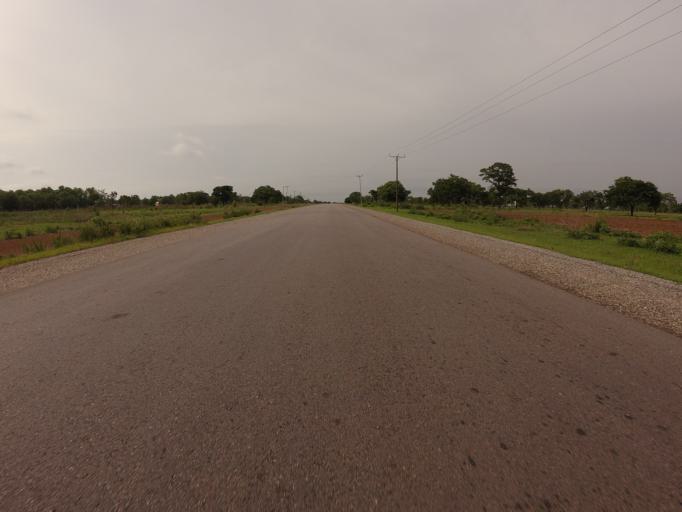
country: GH
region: Northern
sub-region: Yendi
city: Yendi
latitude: 9.6135
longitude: -0.0462
